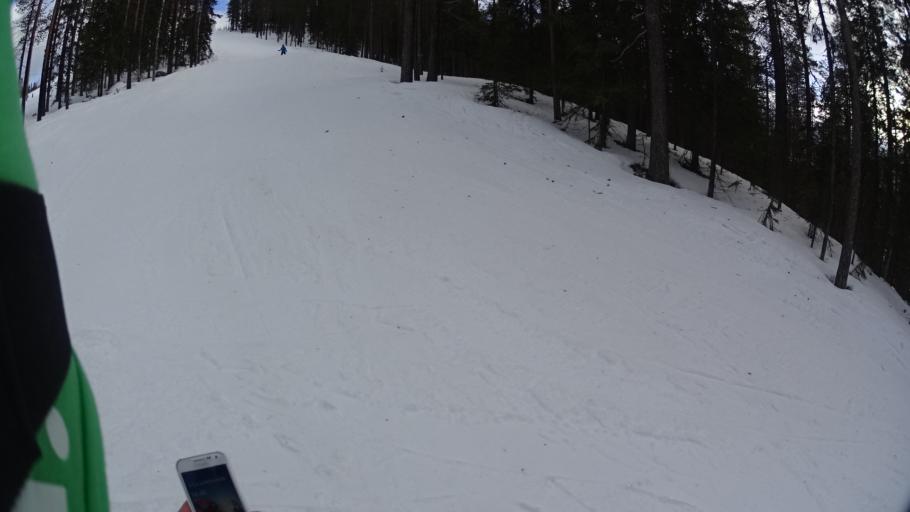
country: SE
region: Vaesterbotten
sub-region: Mala Kommun
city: Mala
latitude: 65.1779
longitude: 18.7584
